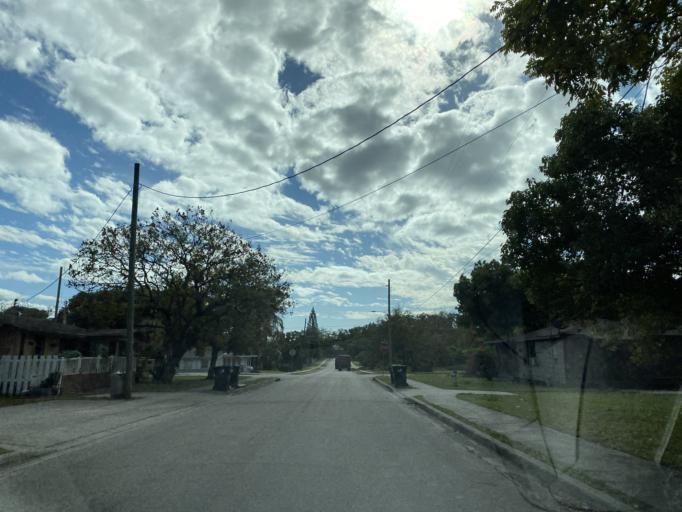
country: US
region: Florida
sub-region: Orange County
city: Holden Heights
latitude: 28.5188
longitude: -81.3909
